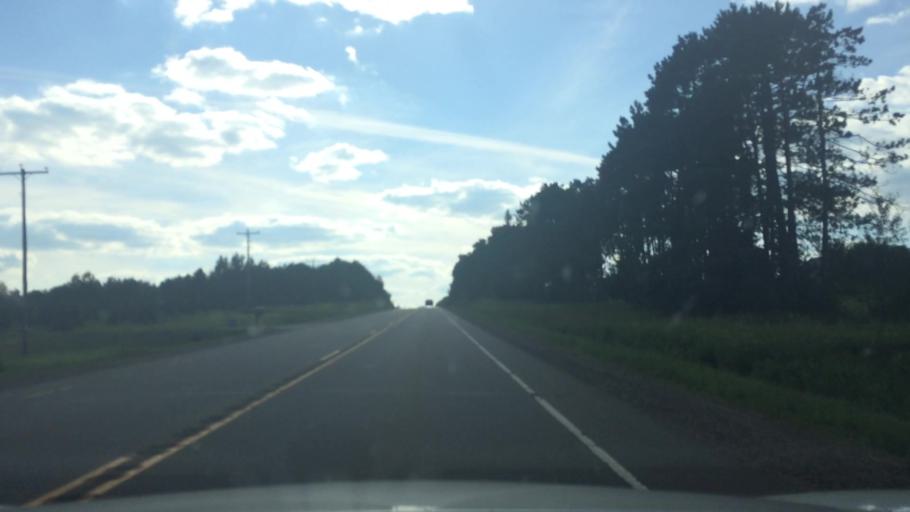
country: US
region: Wisconsin
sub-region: Lincoln County
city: Merrill
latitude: 45.1781
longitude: -89.5969
